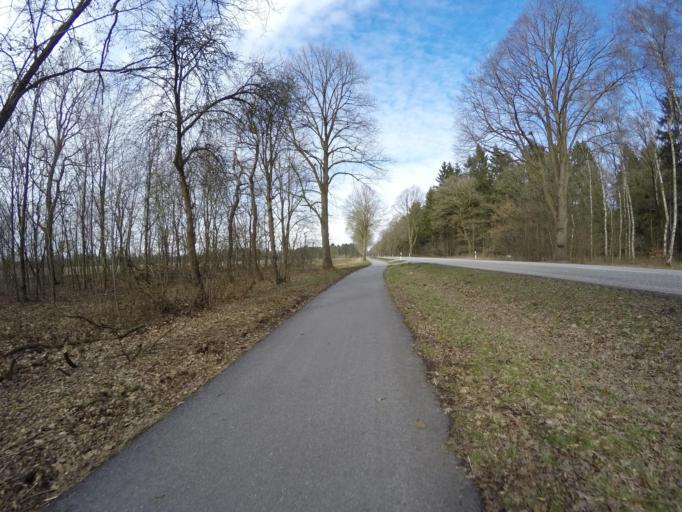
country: DE
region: Schleswig-Holstein
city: Heidmoor
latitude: 53.8169
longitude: 9.8810
